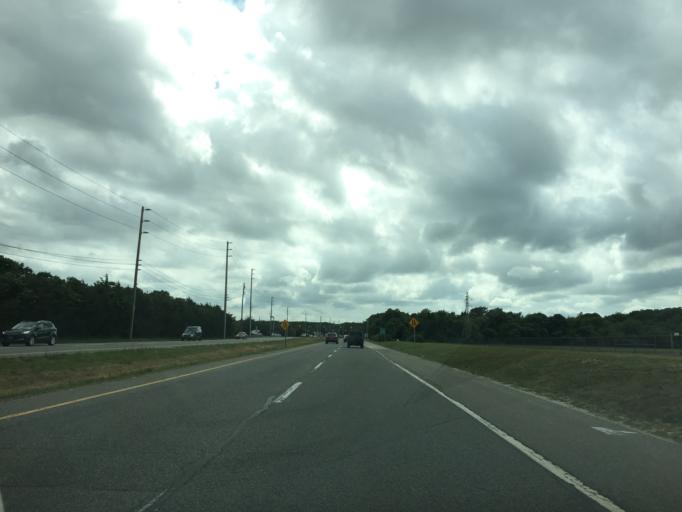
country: US
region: New York
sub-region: Suffolk County
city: Mattituck
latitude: 40.9890
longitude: -72.5480
